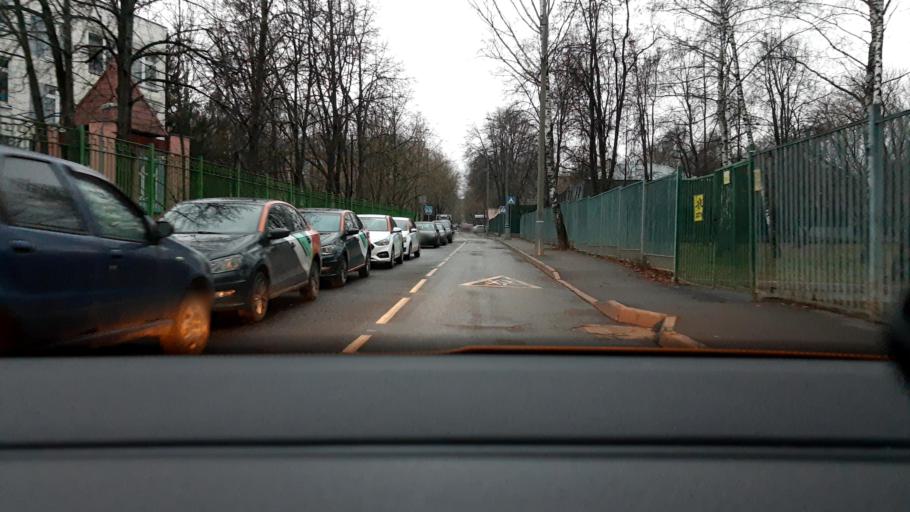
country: RU
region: Moscow
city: Rublevo
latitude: 55.7866
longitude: 37.3628
